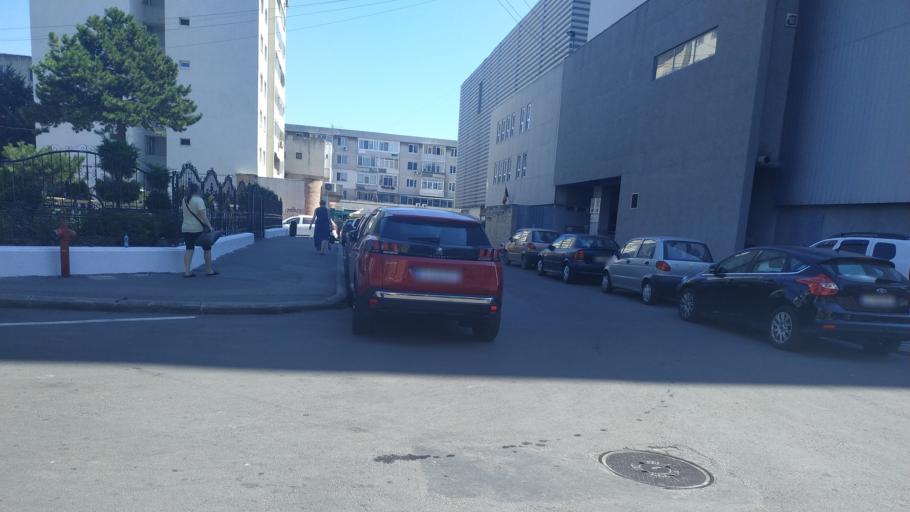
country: RO
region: Constanta
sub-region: Municipiul Constanta
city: Constanta
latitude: 44.1792
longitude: 28.6467
